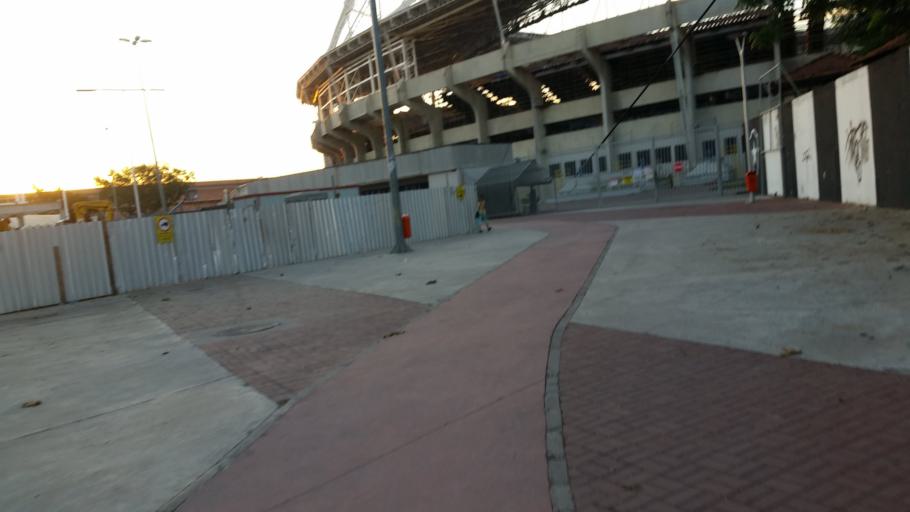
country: BR
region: Rio de Janeiro
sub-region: Rio De Janeiro
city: Rio de Janeiro
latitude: -22.8953
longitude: -43.2920
